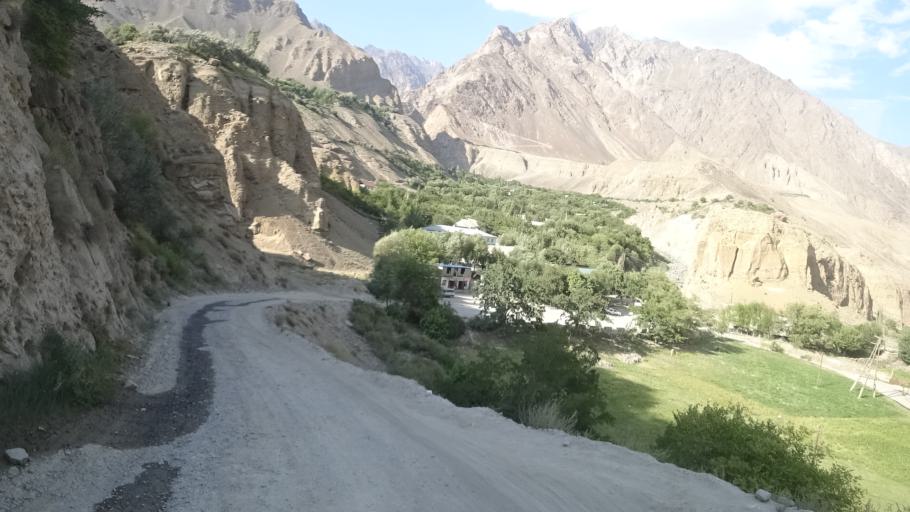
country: TJ
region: Gorno-Badakhshan
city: Vanj
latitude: 38.3156
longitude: 71.2708
